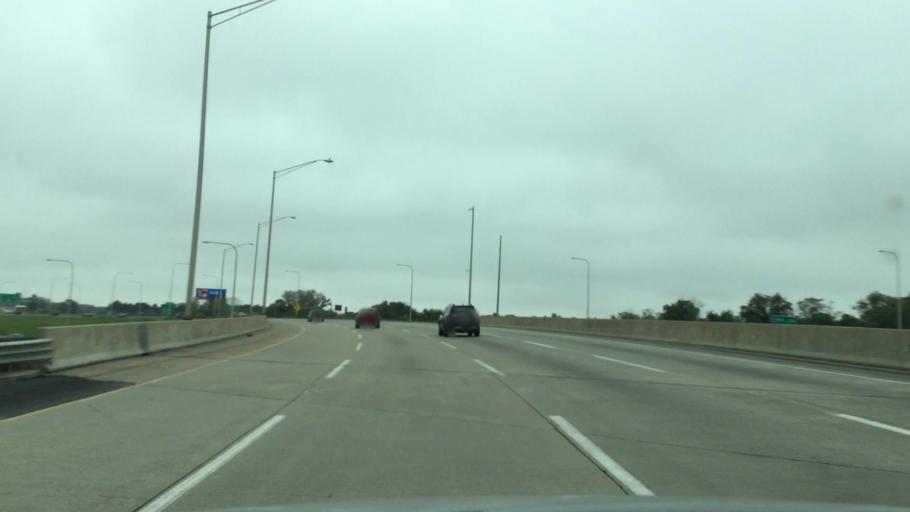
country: US
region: Illinois
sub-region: Lake County
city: Wadsworth
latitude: 42.4788
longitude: -87.9481
